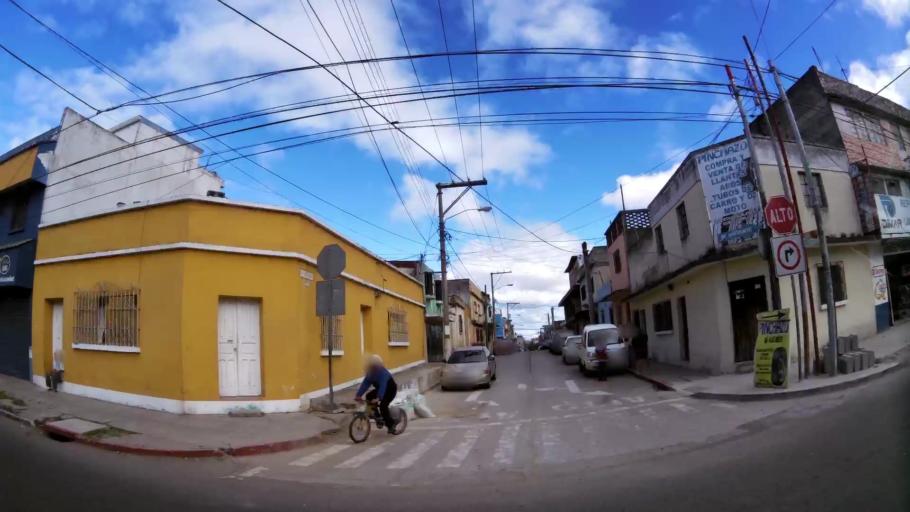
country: GT
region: Guatemala
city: Guatemala City
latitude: 14.6217
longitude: -90.5060
